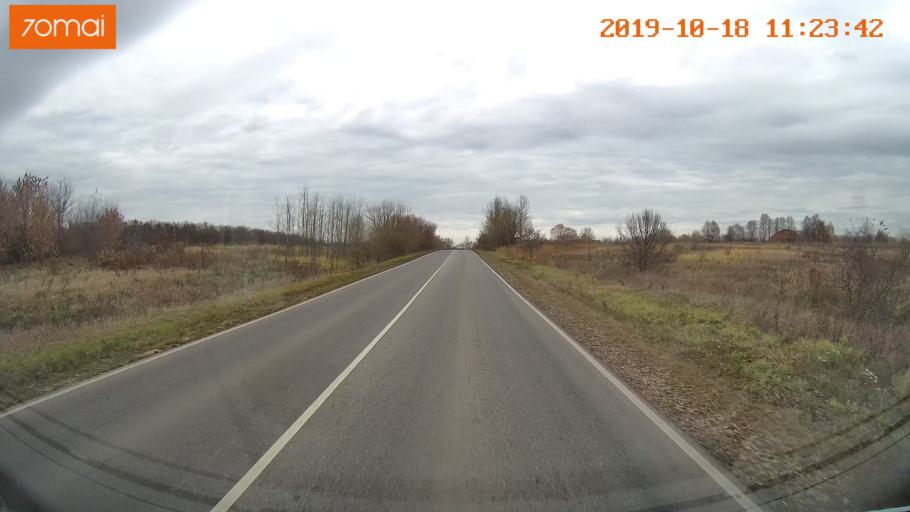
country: RU
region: Tula
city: Kimovsk
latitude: 54.1054
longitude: 38.5948
